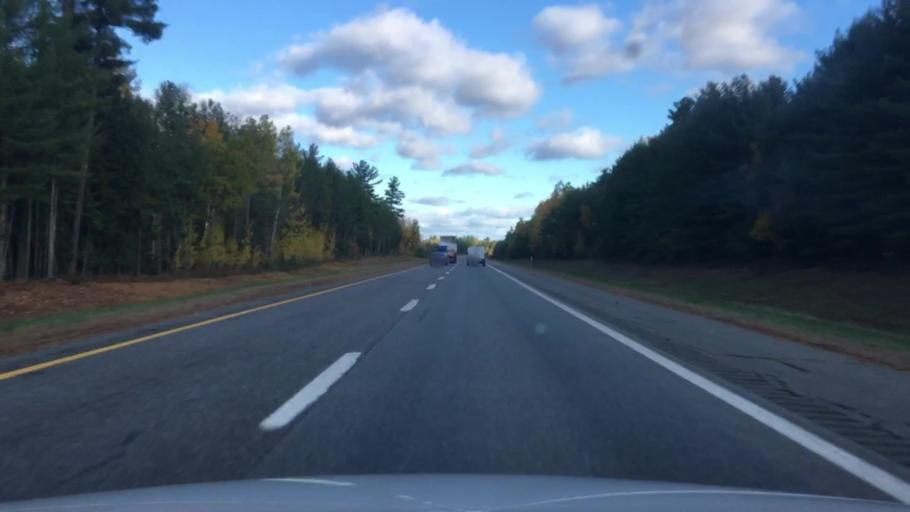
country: US
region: Maine
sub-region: Penobscot County
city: Greenbush
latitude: 45.1416
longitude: -68.7008
